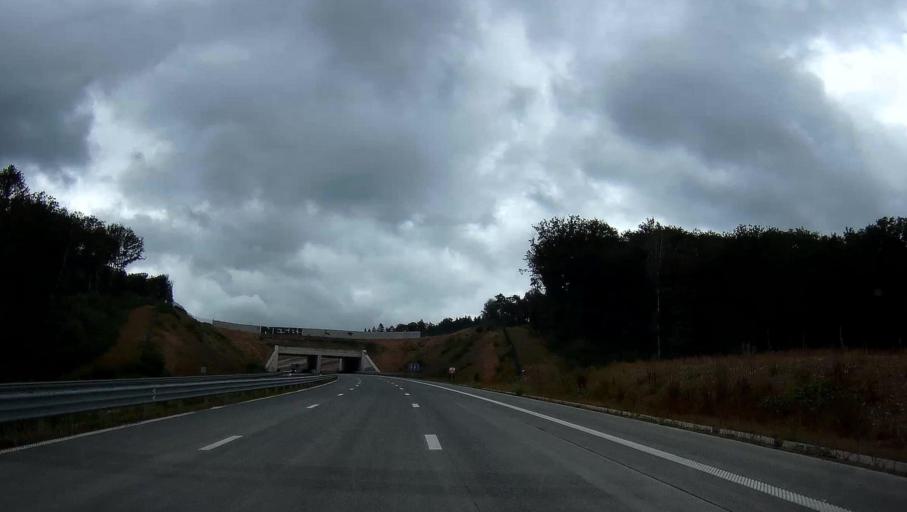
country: BE
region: Wallonia
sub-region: Province de Namur
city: Couvin
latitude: 50.0344
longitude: 4.5075
